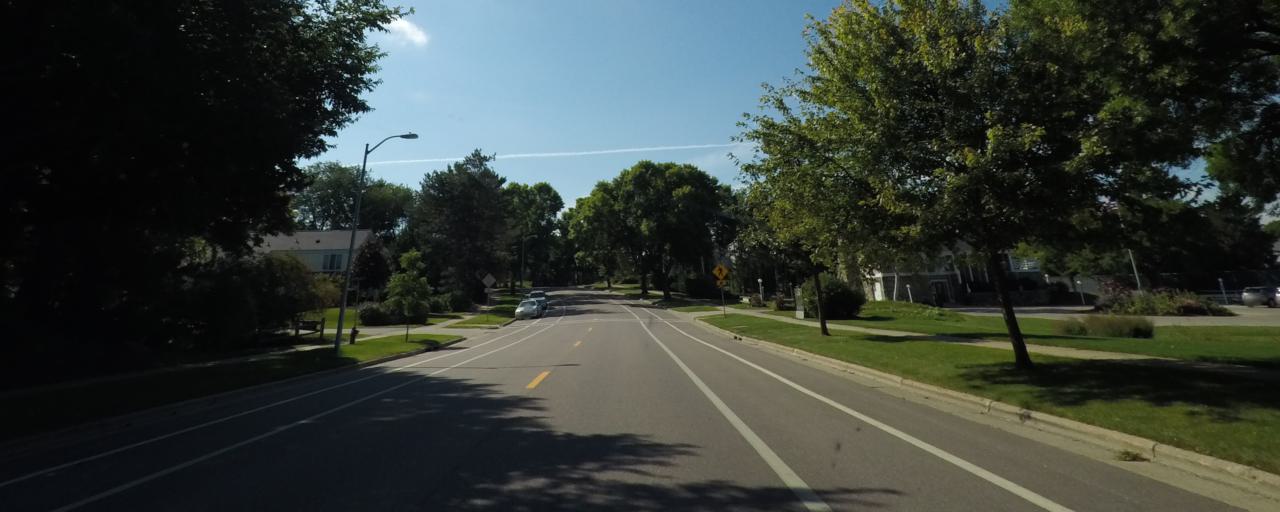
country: US
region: Wisconsin
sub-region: Dane County
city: Middleton
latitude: 43.0662
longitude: -89.5085
